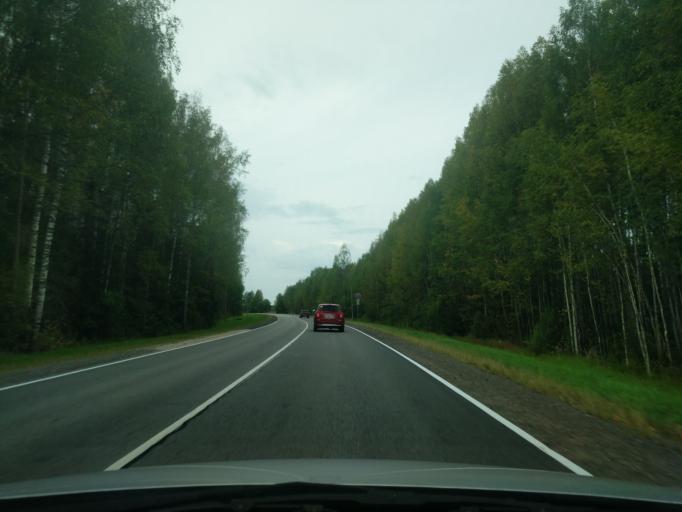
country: RU
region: Kirov
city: Kotel'nich
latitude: 58.2714
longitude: 48.0739
